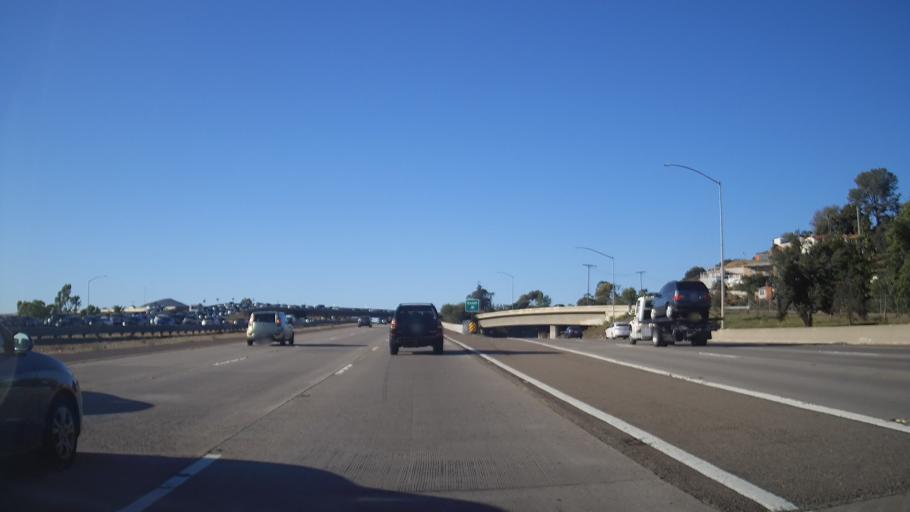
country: US
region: California
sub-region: San Diego County
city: La Mesa
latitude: 32.7736
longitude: -117.0022
